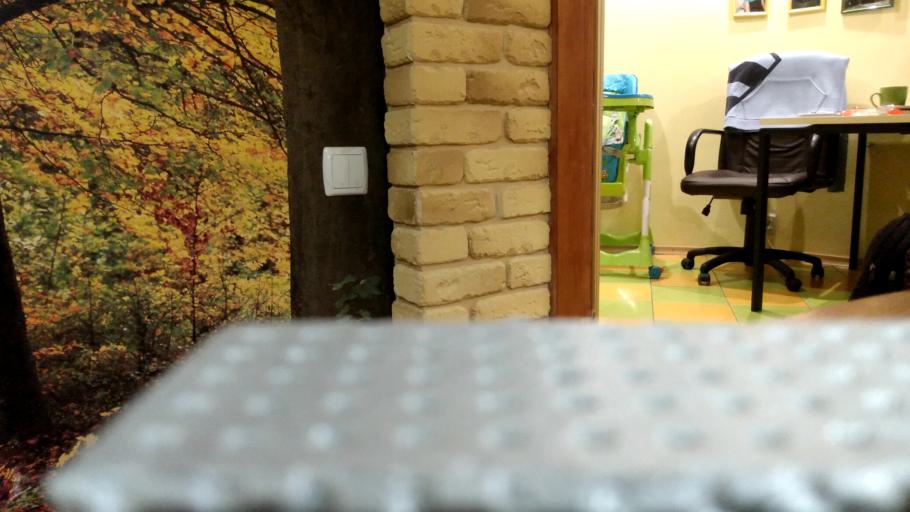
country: RU
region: Republic of Karelia
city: Pudozh
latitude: 61.9624
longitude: 37.6131
